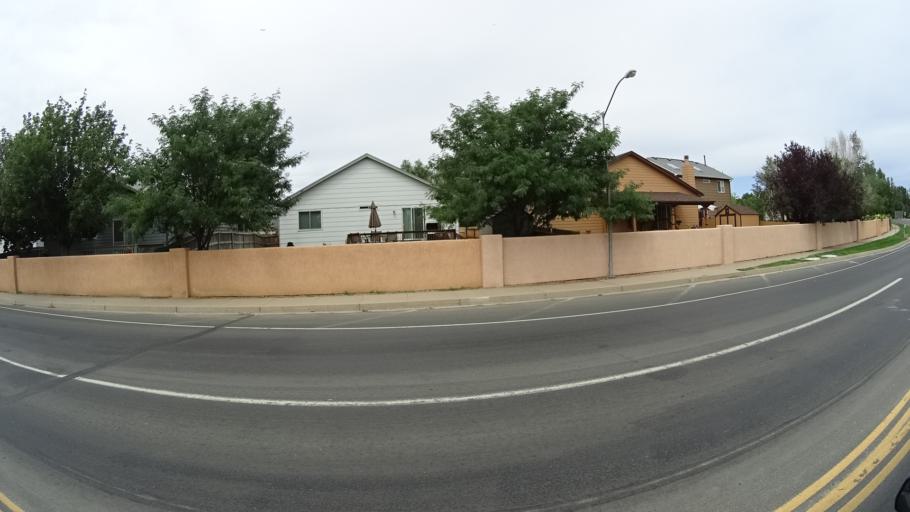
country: US
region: Colorado
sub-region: El Paso County
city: Fountain
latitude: 38.7091
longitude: -104.6968
